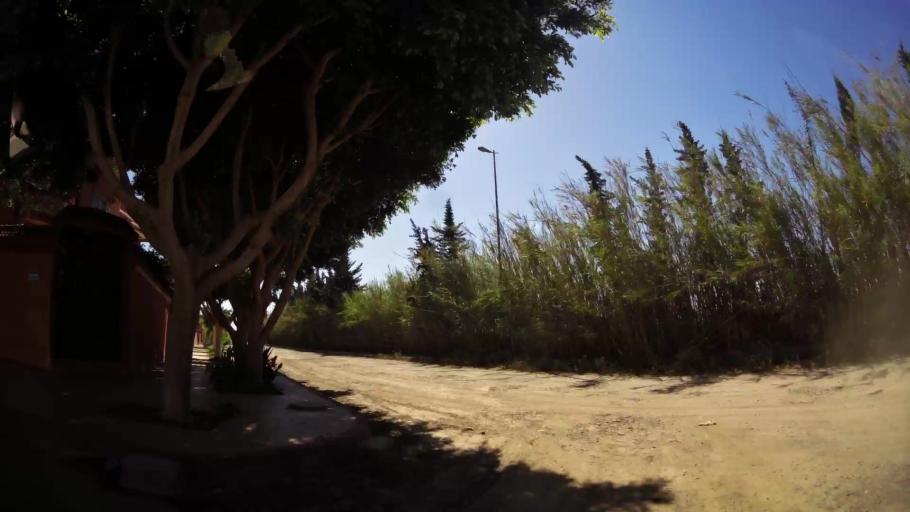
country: MA
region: Oriental
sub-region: Berkane-Taourirt
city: Berkane
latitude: 34.9460
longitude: -2.3293
